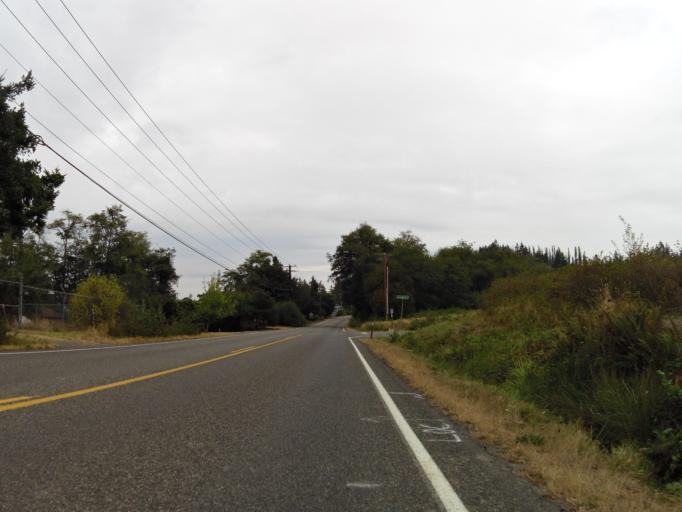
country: US
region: Washington
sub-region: Jefferson County
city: Port Hadlock-Irondale
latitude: 48.0194
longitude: -122.7338
